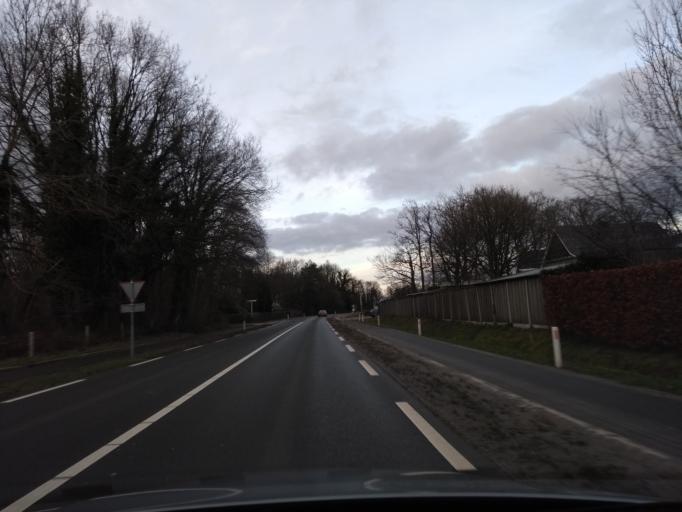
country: NL
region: Overijssel
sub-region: Gemeente Hengelo
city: Hengelo
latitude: 52.3000
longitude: 6.8317
